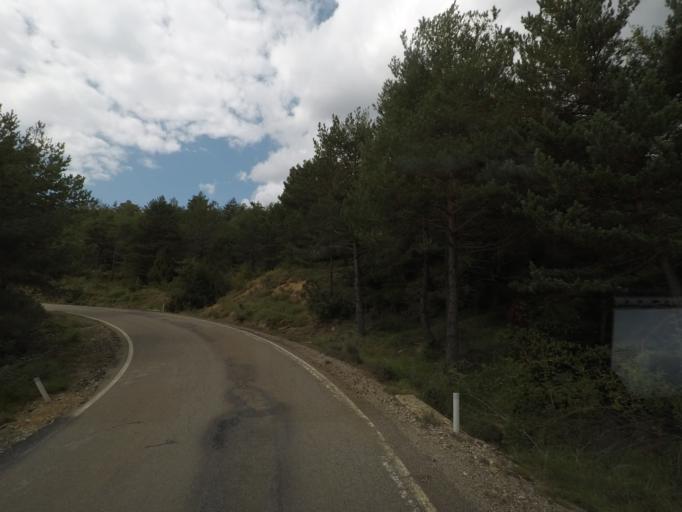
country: ES
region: Aragon
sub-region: Provincia de Huesca
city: Boltana
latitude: 42.4058
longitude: -0.0215
